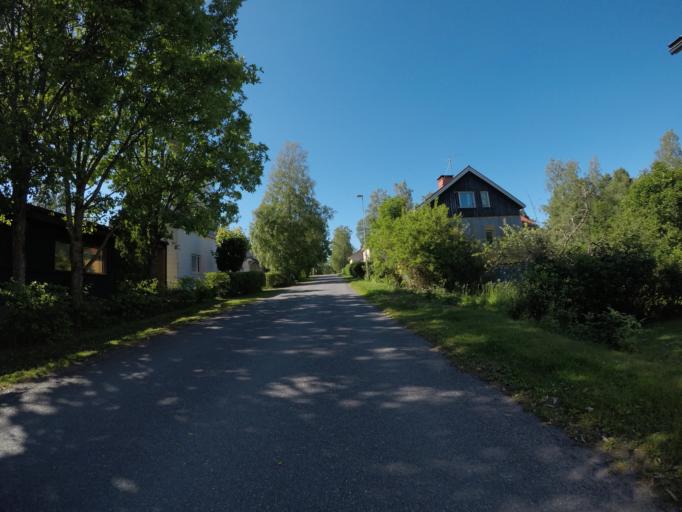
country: FI
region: Haeme
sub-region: Haemeenlinna
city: Haemeenlinna
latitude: 61.0078
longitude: 24.4882
